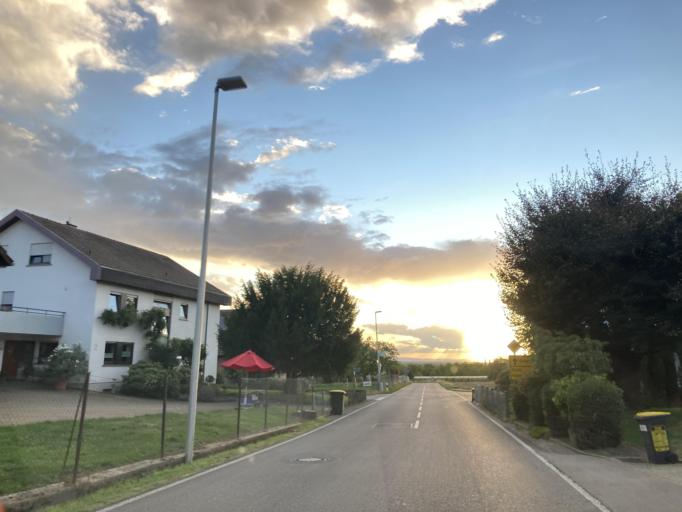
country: DE
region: Baden-Wuerttemberg
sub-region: Freiburg Region
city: Lauf
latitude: 48.6663
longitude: 8.1346
